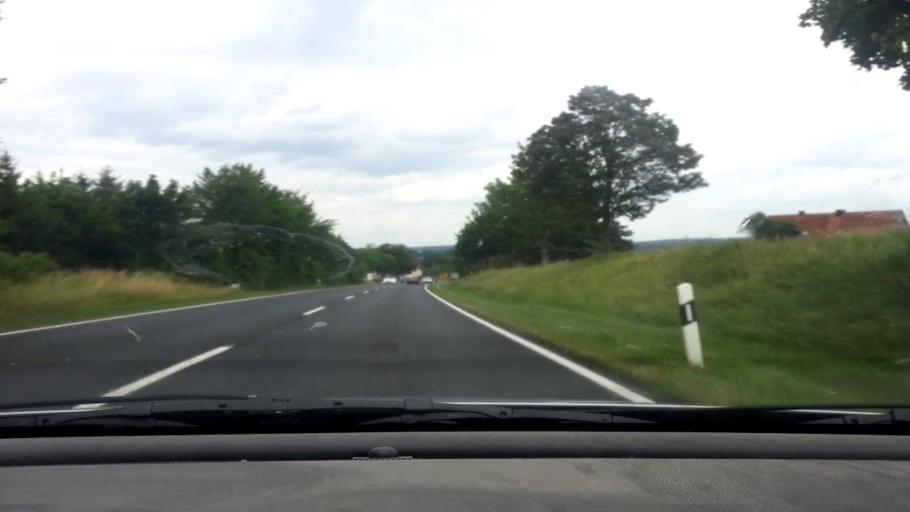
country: DE
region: Bavaria
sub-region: Upper Palatinate
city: Waldsassen
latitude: 49.9885
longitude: 12.2831
